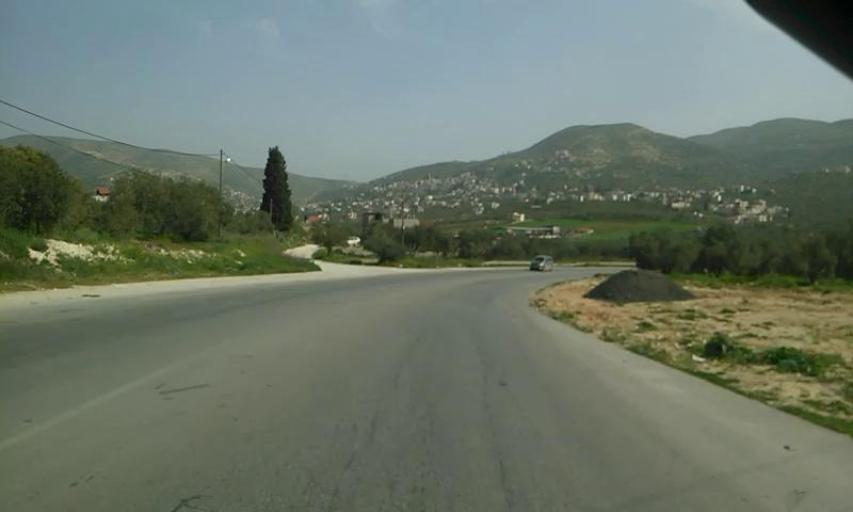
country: PS
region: West Bank
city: Al Fandaqumiyah
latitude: 32.3374
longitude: 35.2061
